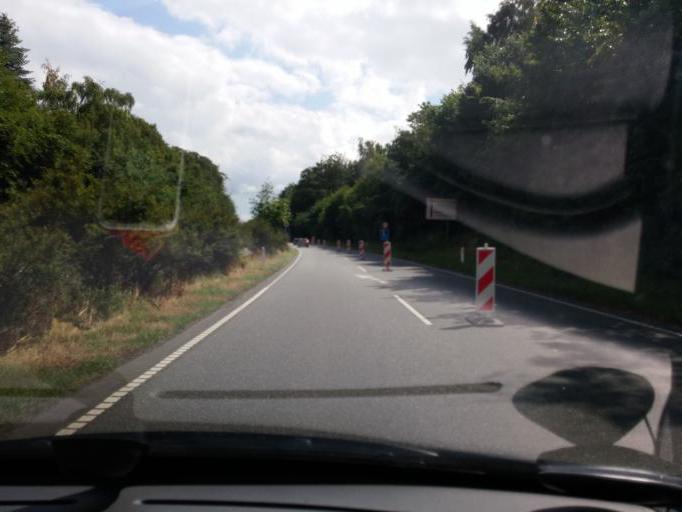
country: DK
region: South Denmark
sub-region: Svendborg Kommune
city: Svendborg
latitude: 55.0562
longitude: 10.5908
